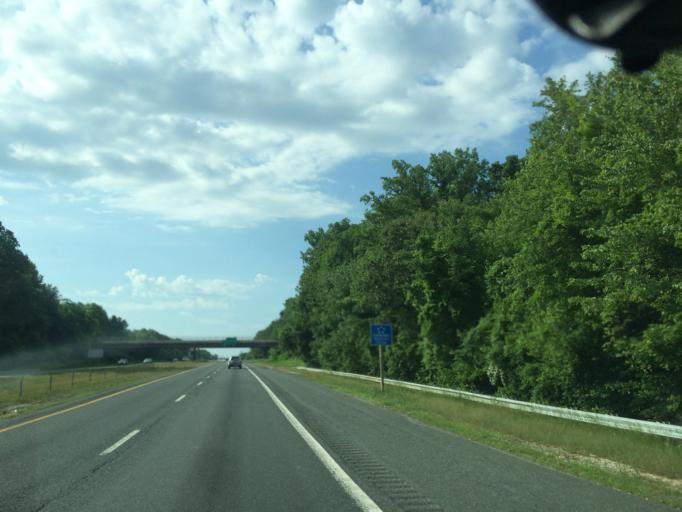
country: US
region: Maryland
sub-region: Baltimore County
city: Reisterstown
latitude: 39.4606
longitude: -76.8367
